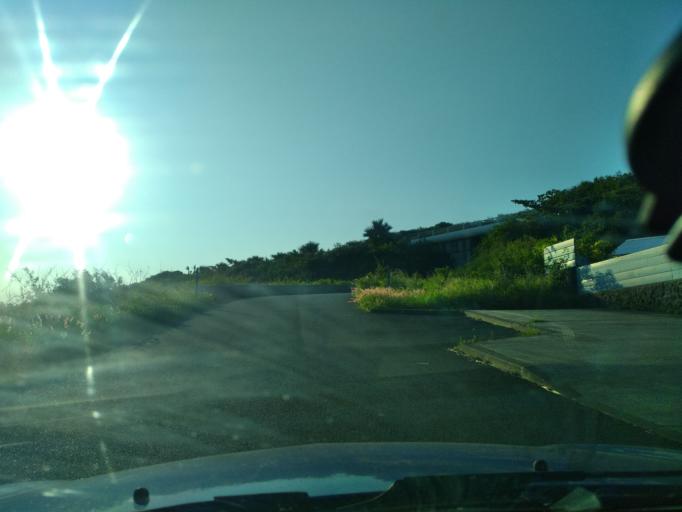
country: RE
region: Reunion
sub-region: Reunion
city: Petite-Ile
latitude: -21.3551
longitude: 55.5221
